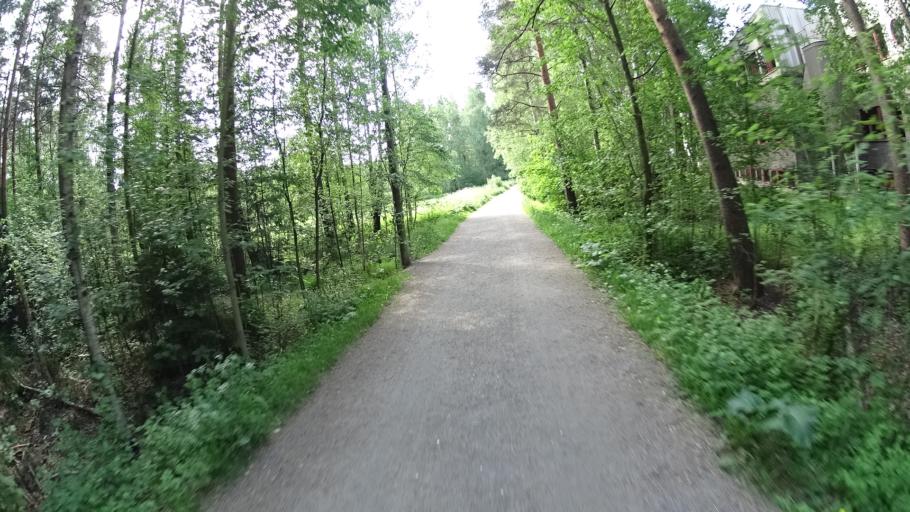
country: FI
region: Uusimaa
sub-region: Helsinki
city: Helsinki
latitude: 60.2034
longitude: 24.9093
